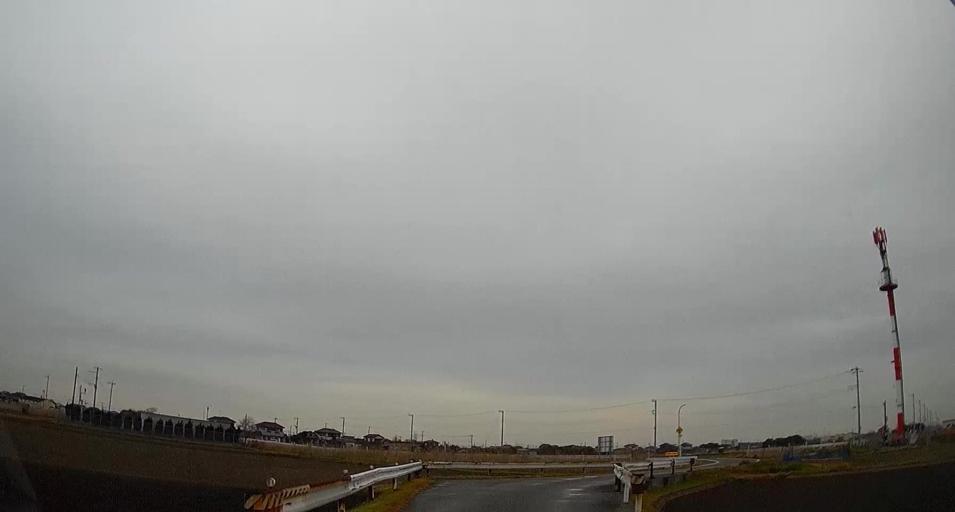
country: JP
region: Chiba
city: Kisarazu
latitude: 35.4242
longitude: 139.9096
